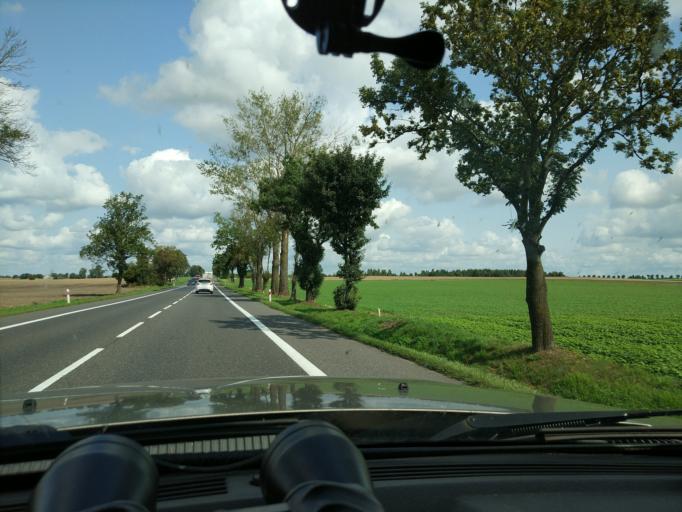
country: PL
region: Masovian Voivodeship
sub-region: Powiat mlawski
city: Wisniewo
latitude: 53.0523
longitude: 20.3444
